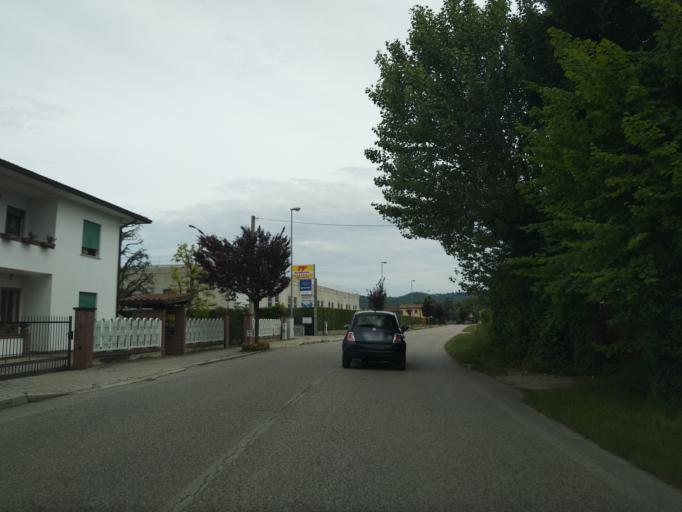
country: IT
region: Veneto
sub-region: Provincia di Padova
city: Montemerlo
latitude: 45.3886
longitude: 11.7014
